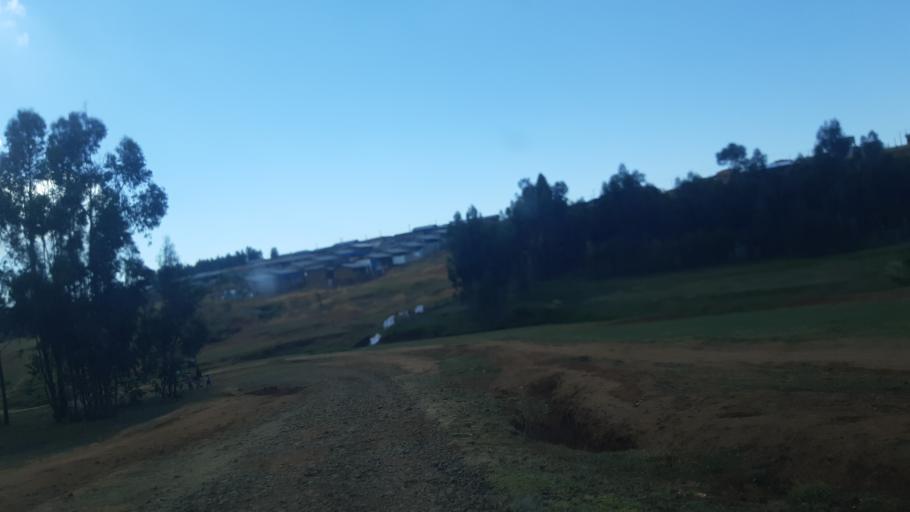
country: ET
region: Amhara
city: Dabat
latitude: 13.3571
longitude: 37.3850
